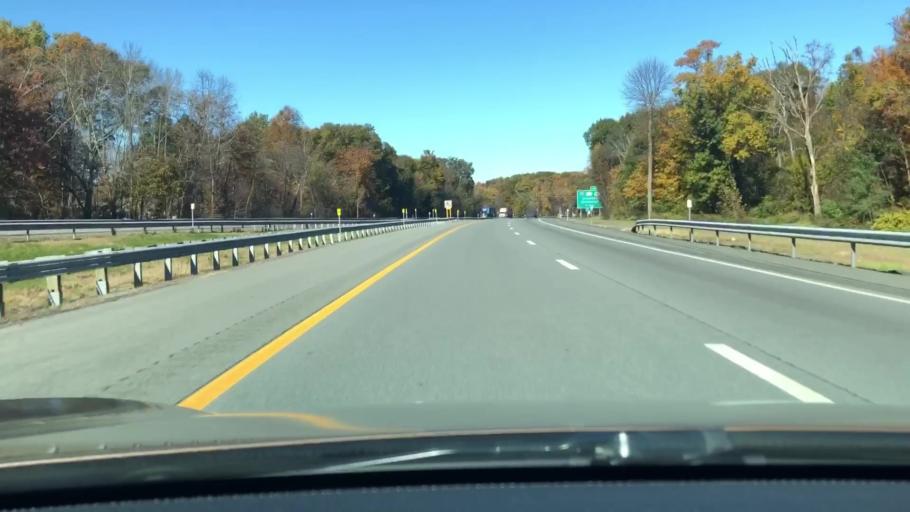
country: US
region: New York
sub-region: Orange County
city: Vails Gate
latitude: 41.4820
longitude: -74.0790
